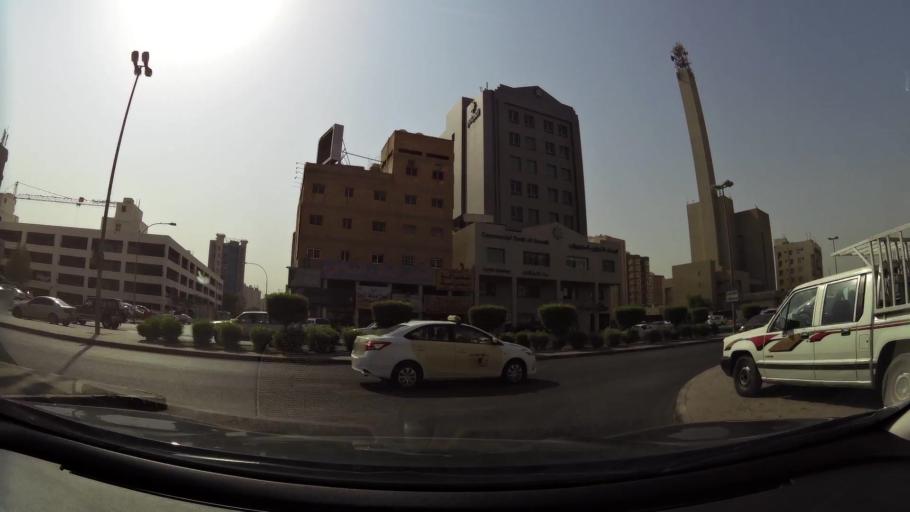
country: KW
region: Muhafazat Hawalli
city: Hawalli
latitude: 29.3359
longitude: 48.0170
